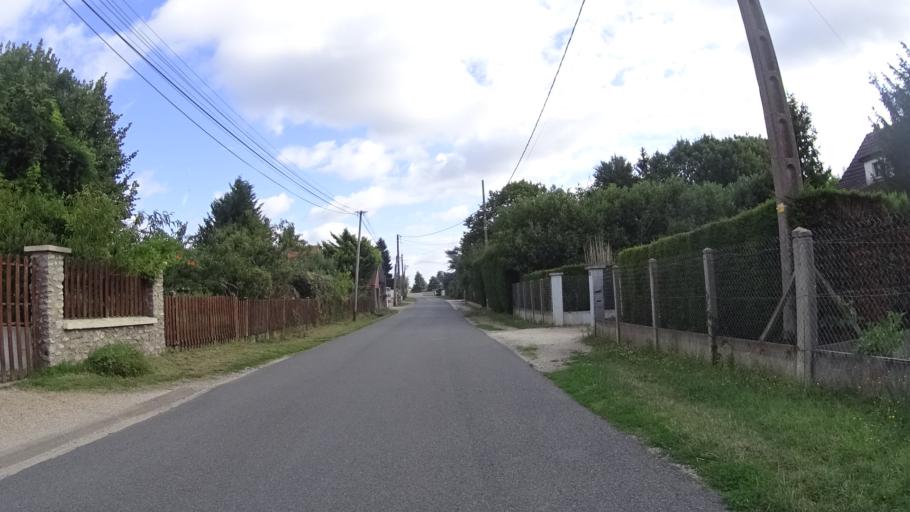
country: FR
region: Centre
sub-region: Departement du Loiret
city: Lorris
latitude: 47.8944
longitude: 2.5129
